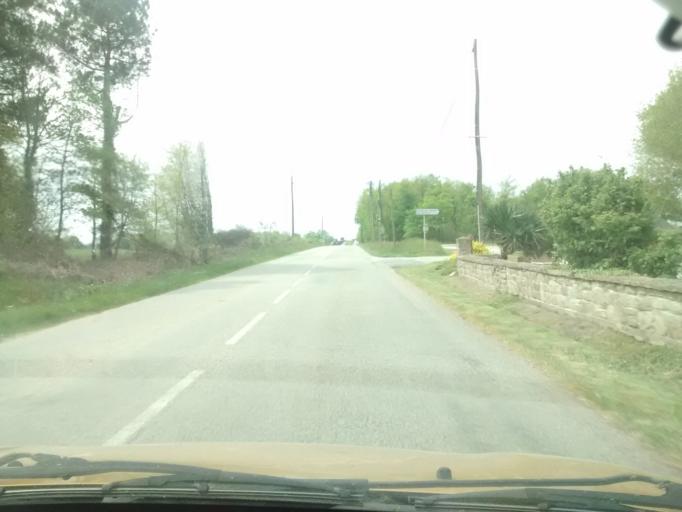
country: FR
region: Brittany
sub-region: Departement du Morbihan
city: Questembert
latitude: 47.6568
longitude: -2.4795
